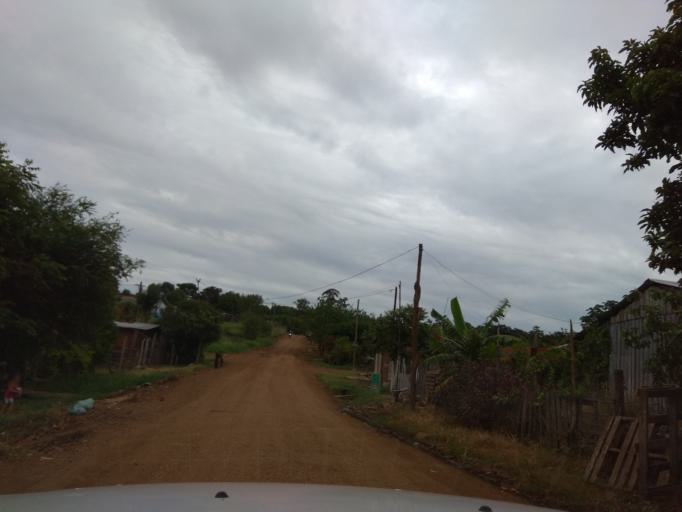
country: AR
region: Misiones
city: Garupa
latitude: -27.4371
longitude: -55.8639
